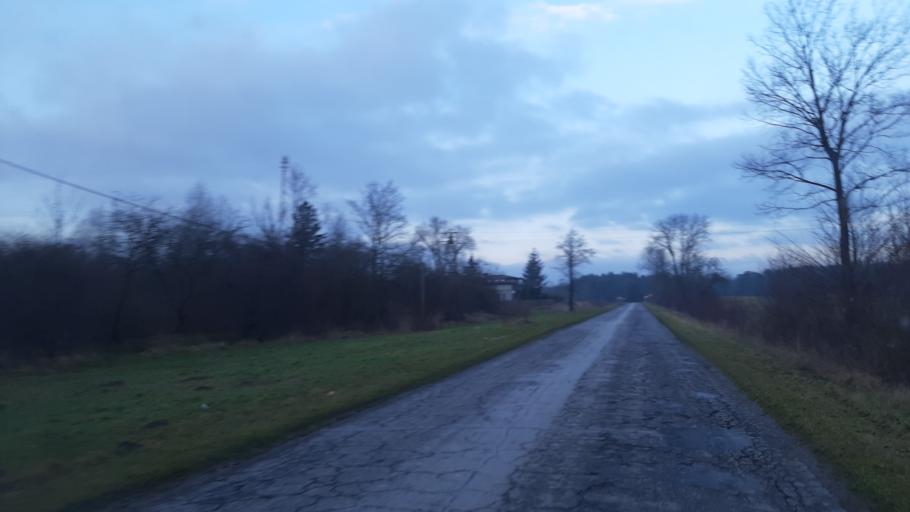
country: PL
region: Lublin Voivodeship
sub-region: Powiat lubartowski
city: Kamionka
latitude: 51.4753
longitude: 22.4670
